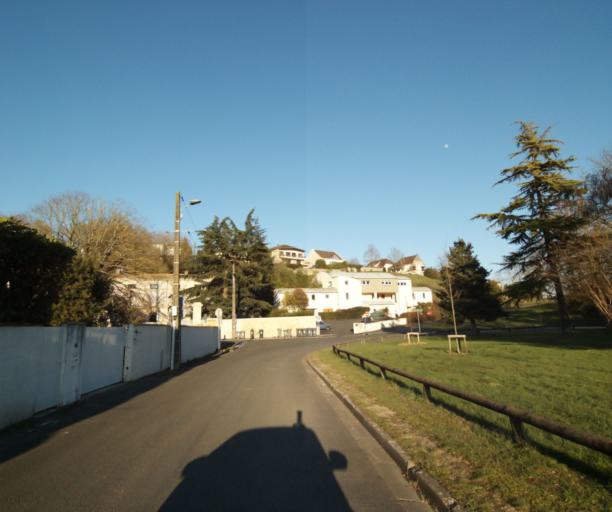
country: FR
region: Poitou-Charentes
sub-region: Departement des Deux-Sevres
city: Niort
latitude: 46.3349
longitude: -0.4787
